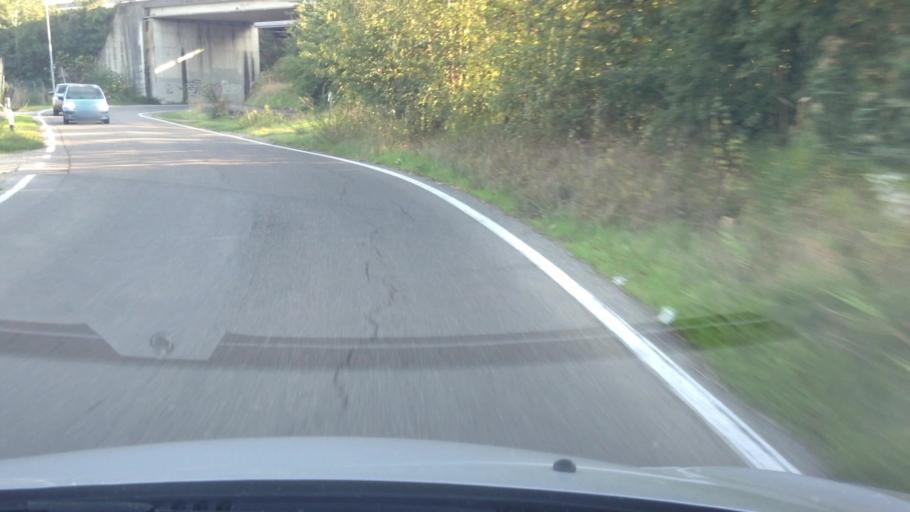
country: IT
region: Emilia-Romagna
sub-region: Provincia di Modena
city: Baggiovara
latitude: 44.6178
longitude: 10.8887
